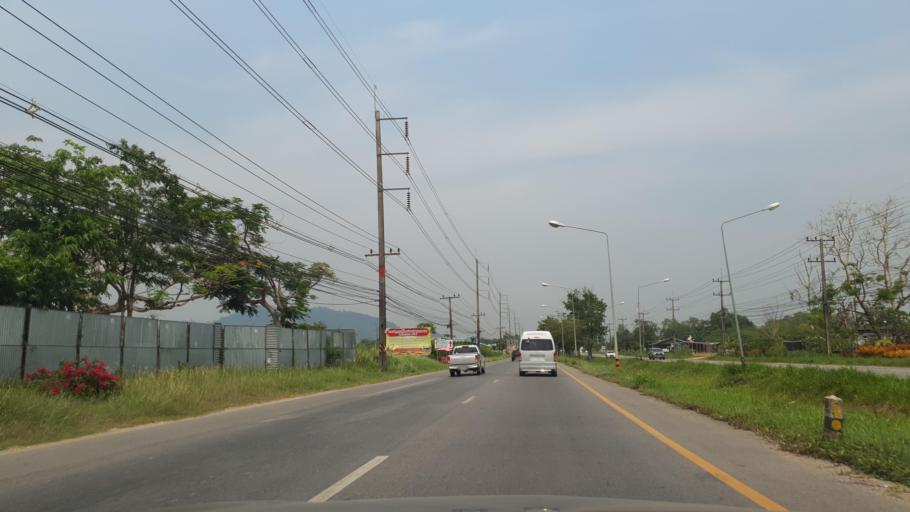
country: TH
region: Rayong
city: Rayong
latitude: 12.6399
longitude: 101.3855
